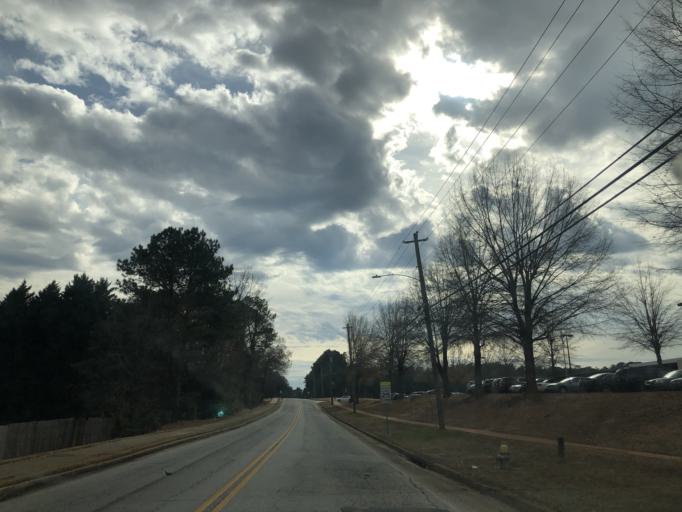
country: US
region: Georgia
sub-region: DeKalb County
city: Panthersville
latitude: 33.6806
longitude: -84.2151
